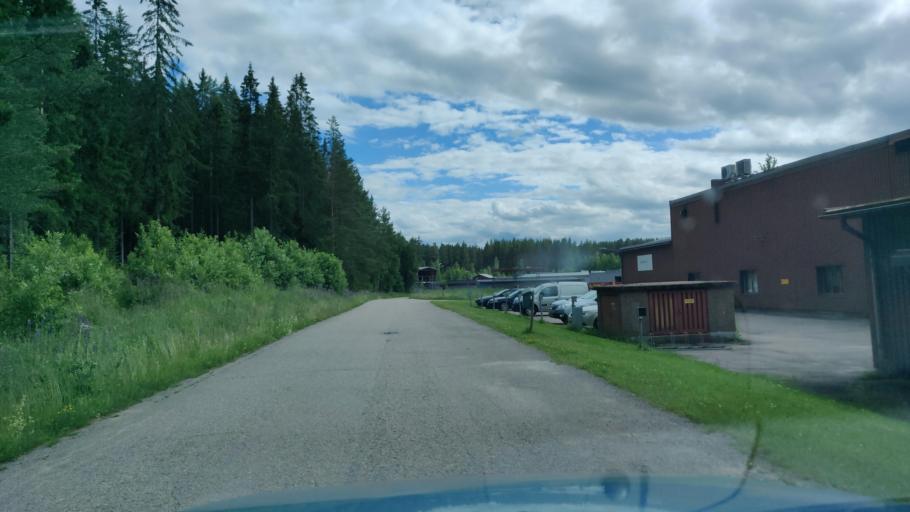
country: SE
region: Vaermland
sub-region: Hagfors Kommun
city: Hagfors
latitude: 60.0462
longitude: 13.7122
